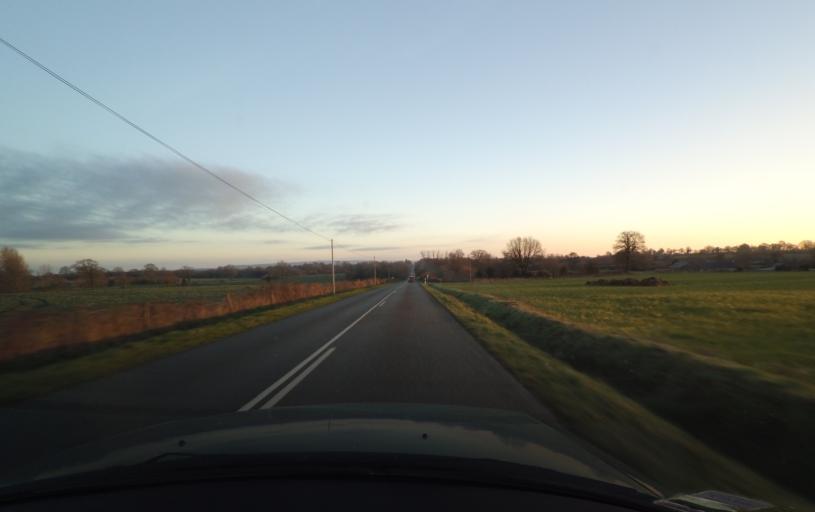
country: FR
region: Pays de la Loire
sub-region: Departement de la Mayenne
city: Bais
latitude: 48.3015
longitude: -0.3454
